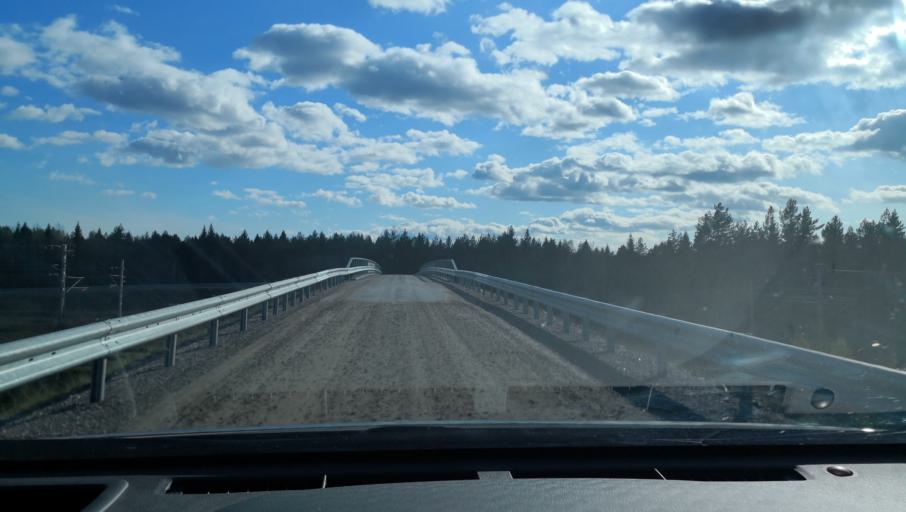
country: SE
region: OErebro
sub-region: Askersunds Kommun
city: Asbro
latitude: 58.8993
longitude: 15.1046
